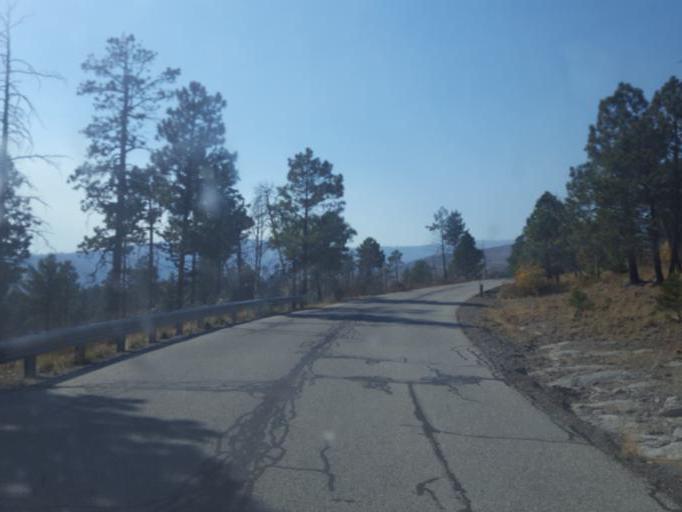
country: US
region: New Mexico
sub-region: Los Alamos County
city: Los Alamos
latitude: 35.8780
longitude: -106.3591
